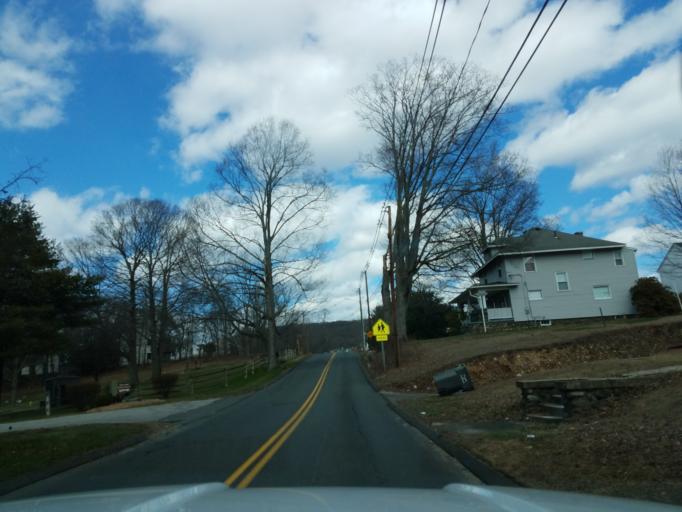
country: US
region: Connecticut
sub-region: New Haven County
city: Naugatuck
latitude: 41.4700
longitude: -73.0466
